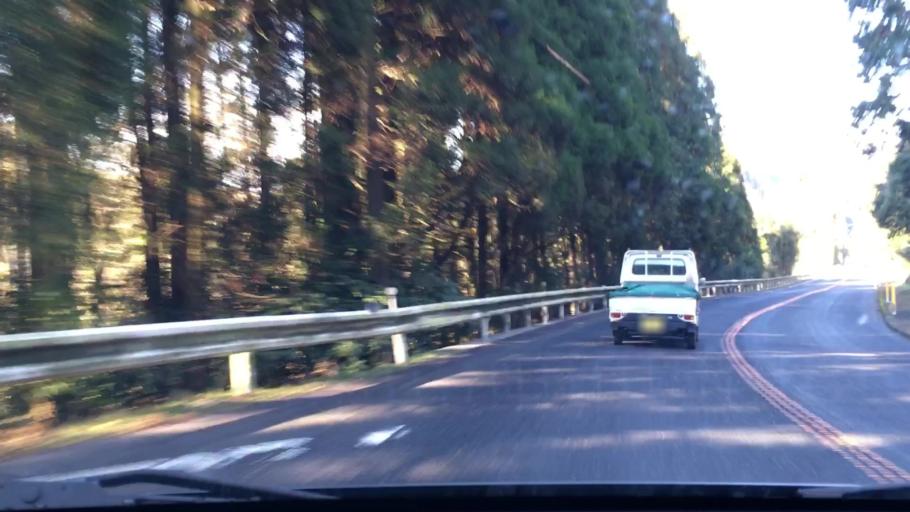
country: JP
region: Kagoshima
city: Sueyoshicho-ninokata
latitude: 31.6627
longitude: 130.9025
